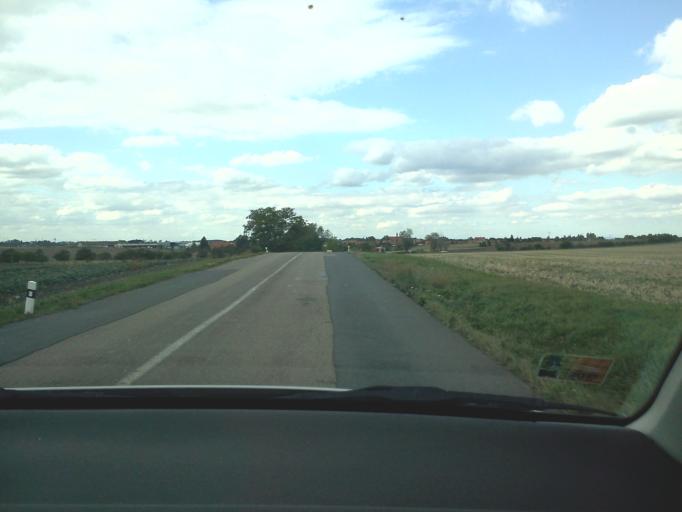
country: CZ
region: Central Bohemia
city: Prerov nad Labem
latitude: 50.1254
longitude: 14.8510
